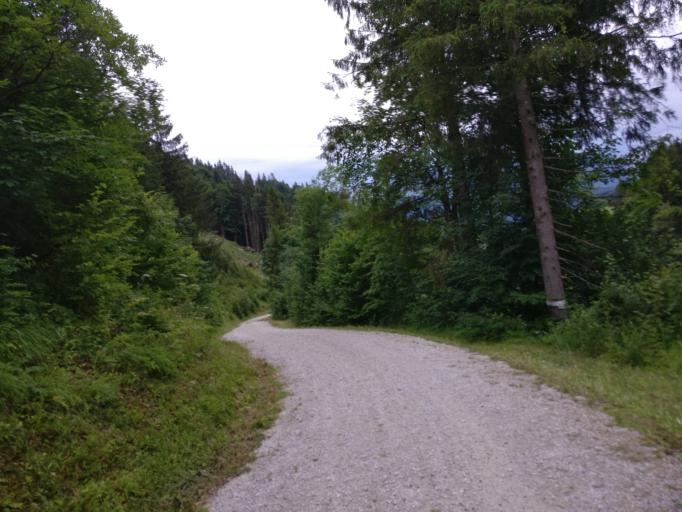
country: AT
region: Tyrol
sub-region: Politischer Bezirk Kitzbuhel
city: Hochfilzen
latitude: 47.4930
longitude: 12.6095
